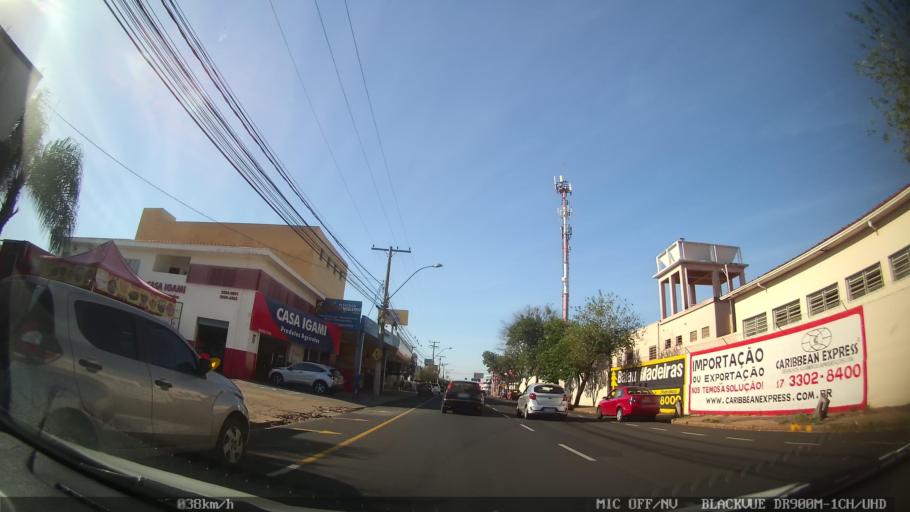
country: BR
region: Sao Paulo
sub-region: Sao Jose Do Rio Preto
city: Sao Jose do Rio Preto
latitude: -20.8009
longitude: -49.3697
